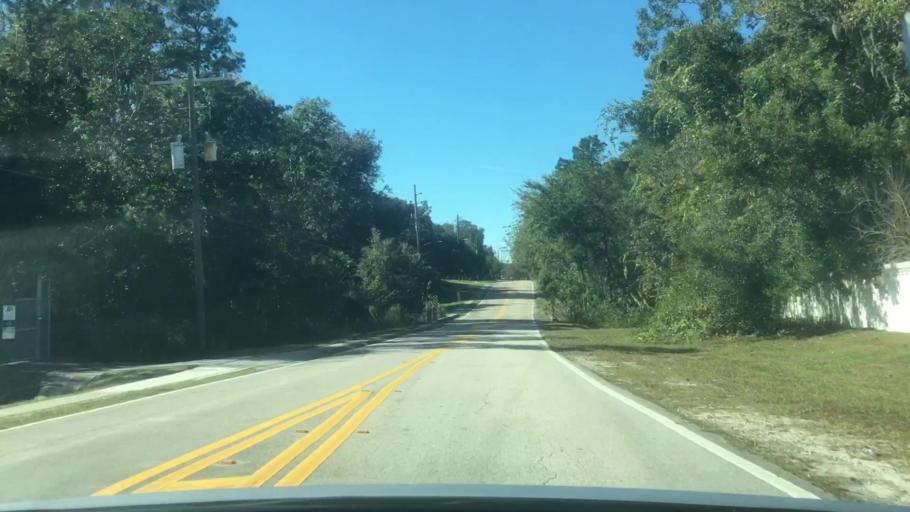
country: US
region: Florida
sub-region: Duval County
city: Jacksonville
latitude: 30.3384
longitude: -81.5302
